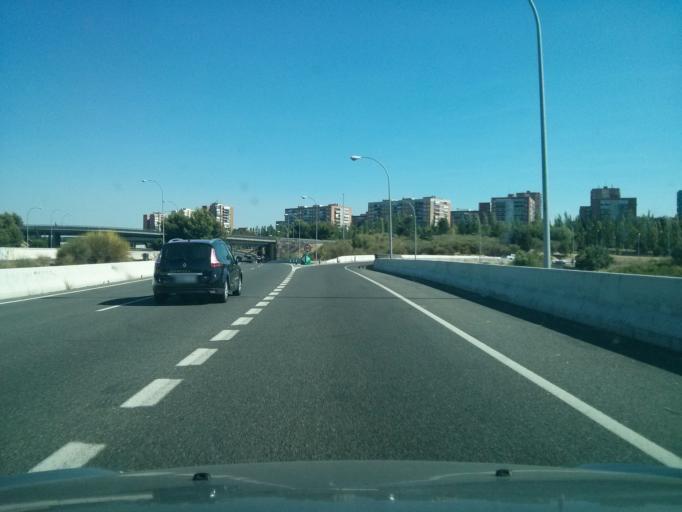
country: ES
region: Madrid
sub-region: Provincia de Madrid
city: Hortaleza
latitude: 40.4825
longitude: -3.6445
